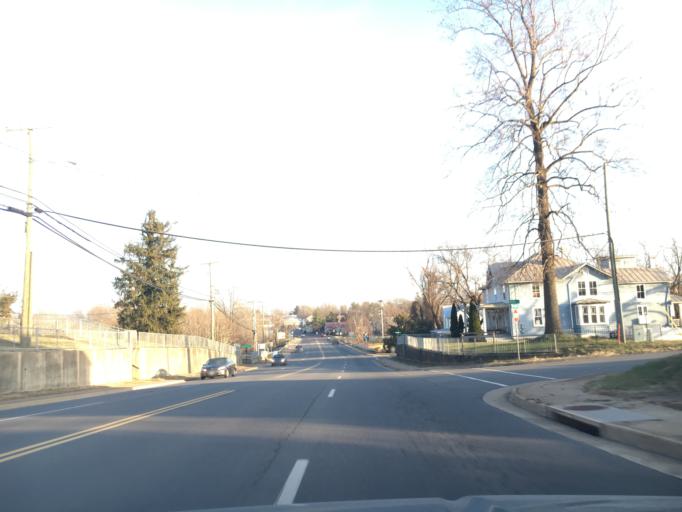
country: US
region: Virginia
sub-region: Culpeper County
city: Culpeper
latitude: 38.4783
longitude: -78.0009
